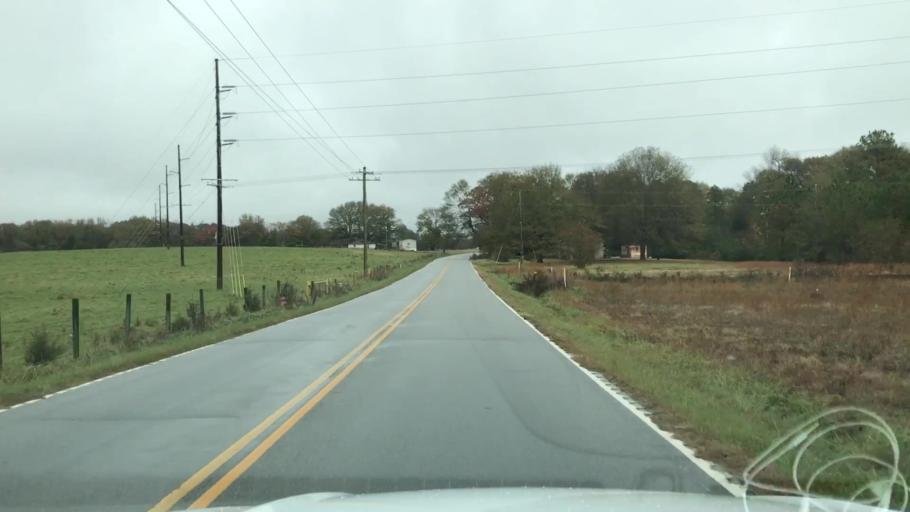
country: US
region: South Carolina
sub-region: Spartanburg County
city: Roebuck
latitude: 34.7884
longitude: -81.9167
